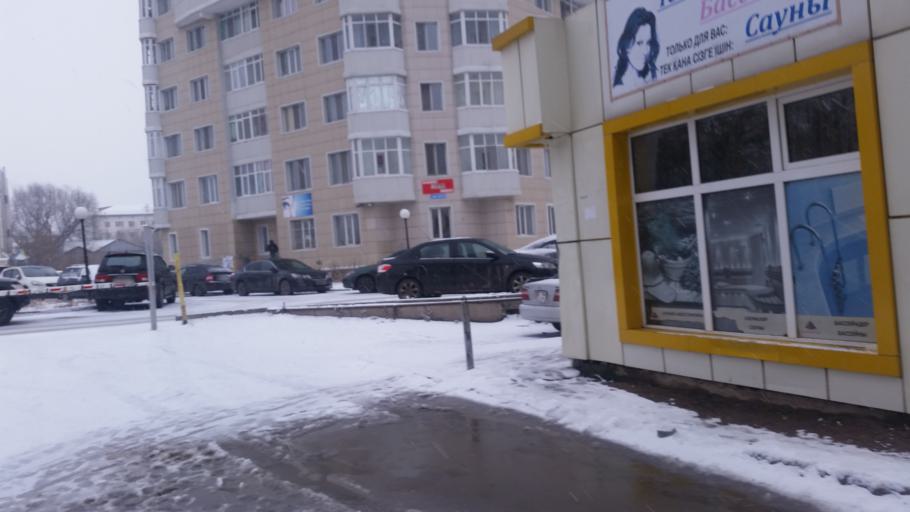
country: KZ
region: Astana Qalasy
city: Astana
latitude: 51.1637
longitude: 71.4659
